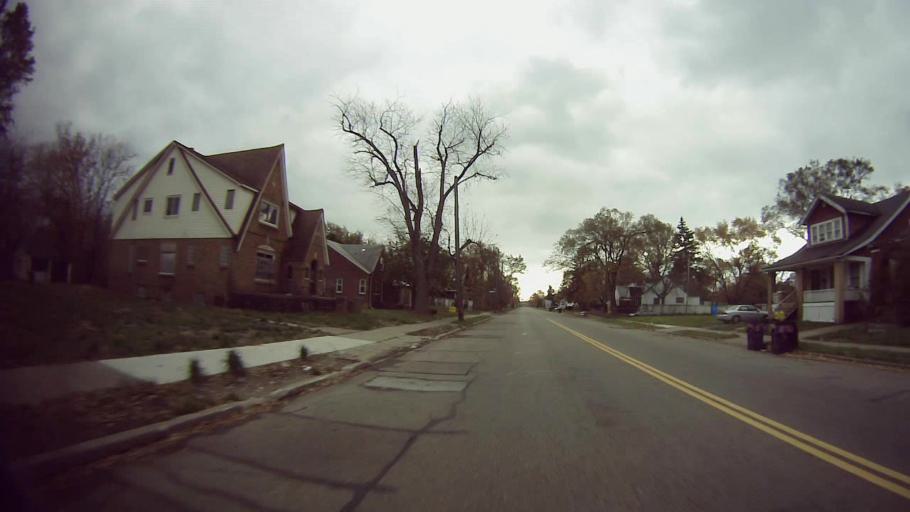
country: US
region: Michigan
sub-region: Macomb County
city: Eastpointe
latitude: 42.4337
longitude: -82.9850
